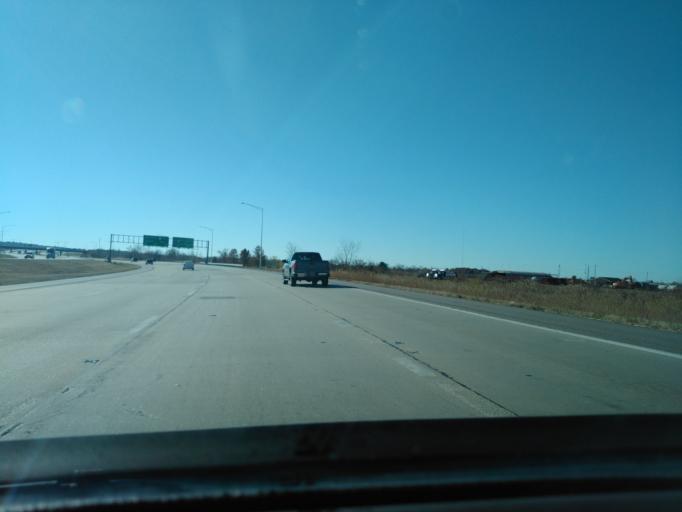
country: US
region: Illinois
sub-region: Saint Clair County
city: Washington Park
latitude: 38.6297
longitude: -90.0669
